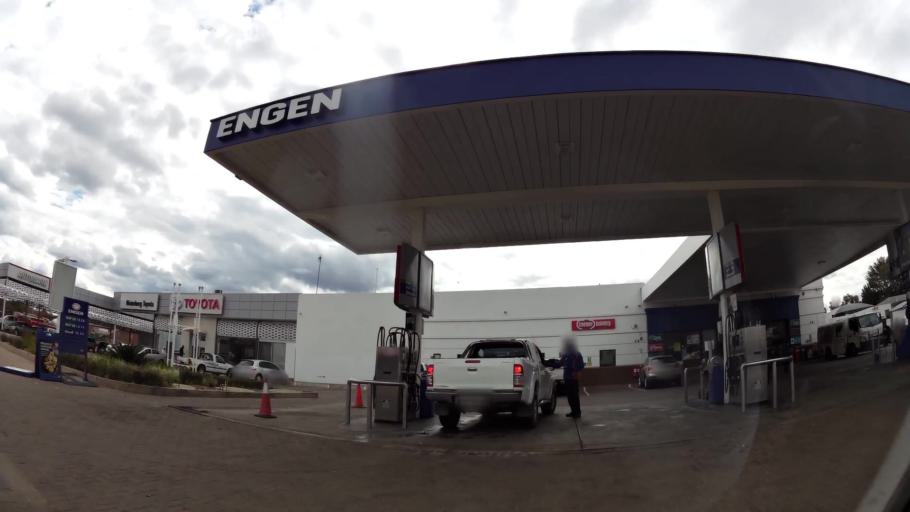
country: ZA
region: Limpopo
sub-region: Waterberg District Municipality
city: Modimolle
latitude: -24.6970
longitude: 28.4093
